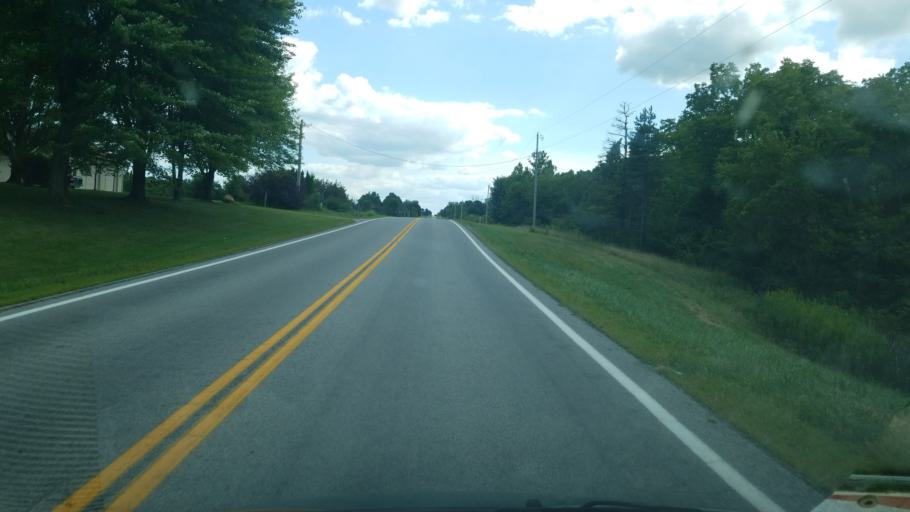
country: US
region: Ohio
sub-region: Allen County
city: Lima
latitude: 40.6668
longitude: -83.9757
